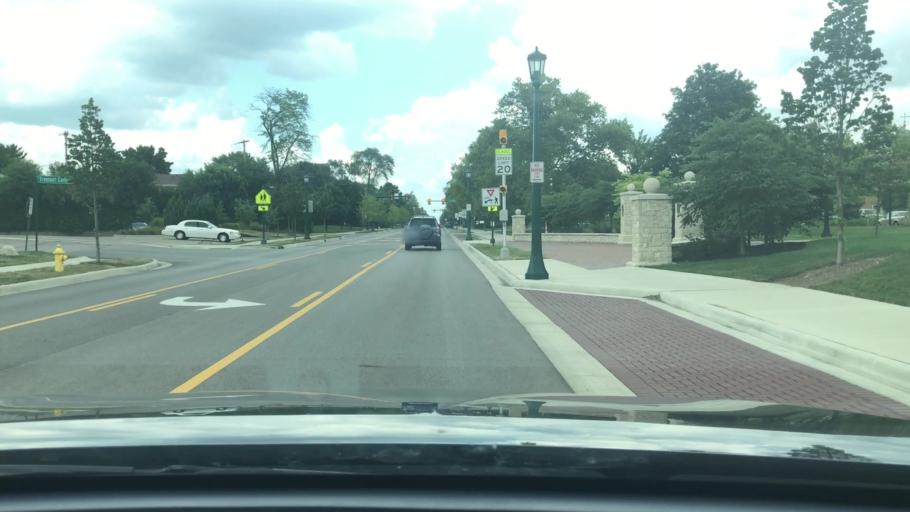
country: US
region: Ohio
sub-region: Franklin County
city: Upper Arlington
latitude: 40.0137
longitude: -83.0675
